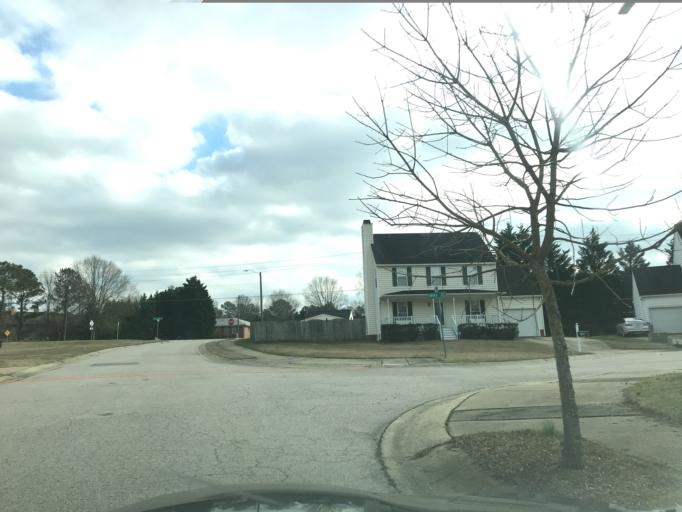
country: US
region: North Carolina
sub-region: Wake County
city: Raleigh
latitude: 35.8189
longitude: -78.5791
